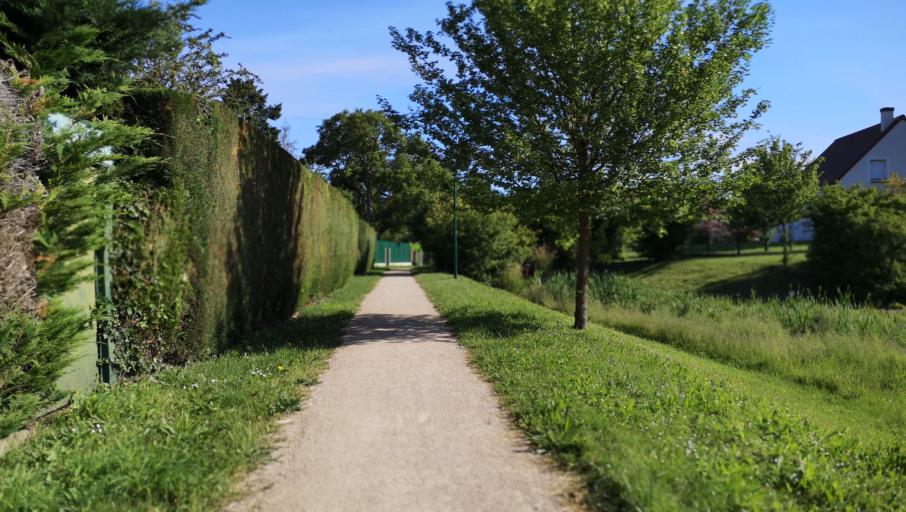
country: FR
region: Centre
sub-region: Departement du Loiret
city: Saint-Jean-de-Braye
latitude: 47.9167
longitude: 1.9727
